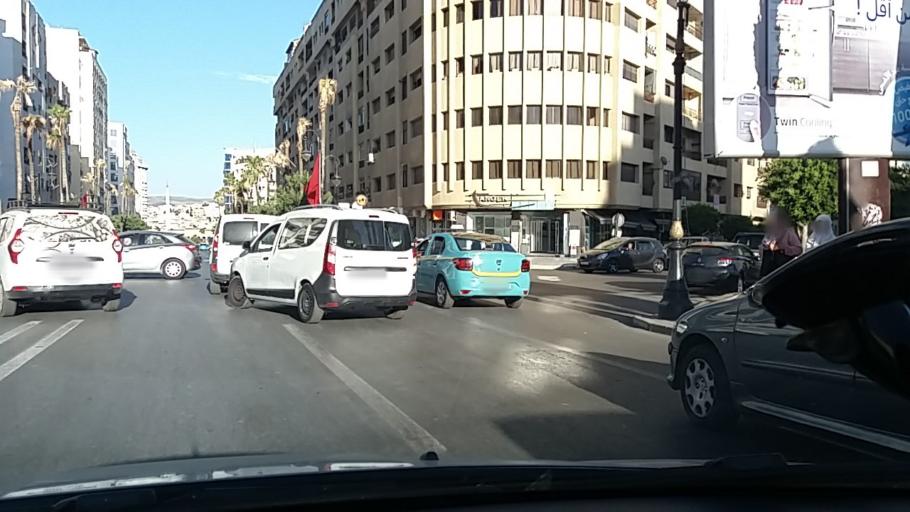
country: MA
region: Tanger-Tetouan
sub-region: Tanger-Assilah
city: Tangier
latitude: 35.7704
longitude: -5.8084
